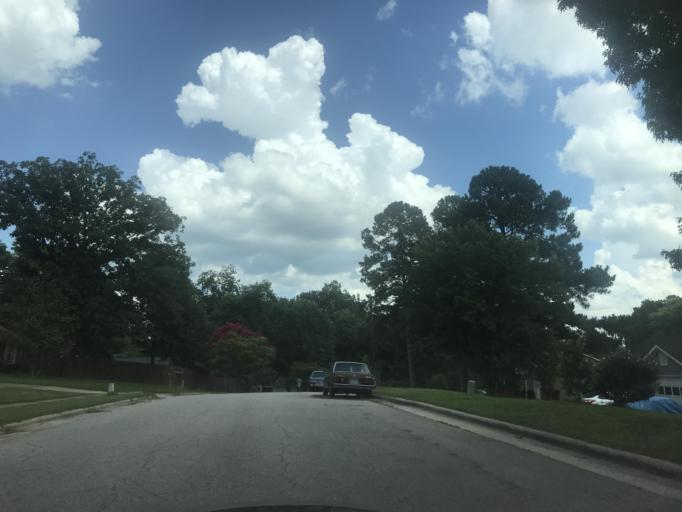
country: US
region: North Carolina
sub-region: Wake County
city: Knightdale
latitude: 35.8541
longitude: -78.5639
